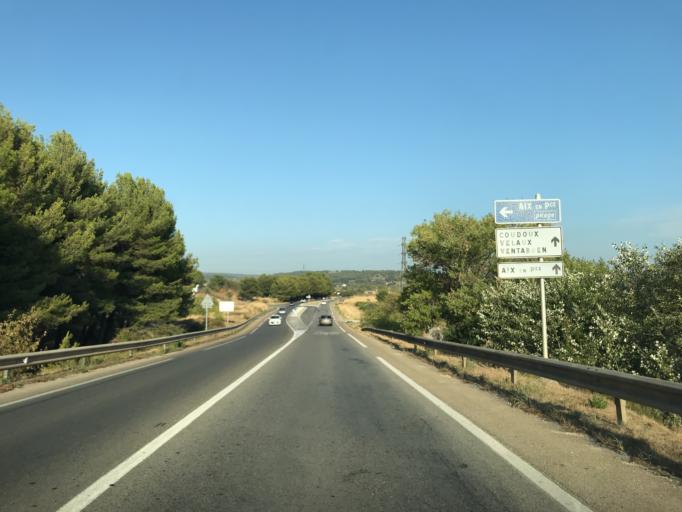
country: FR
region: Provence-Alpes-Cote d'Azur
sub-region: Departement des Bouches-du-Rhone
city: Coudoux
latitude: 43.5502
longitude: 5.2338
